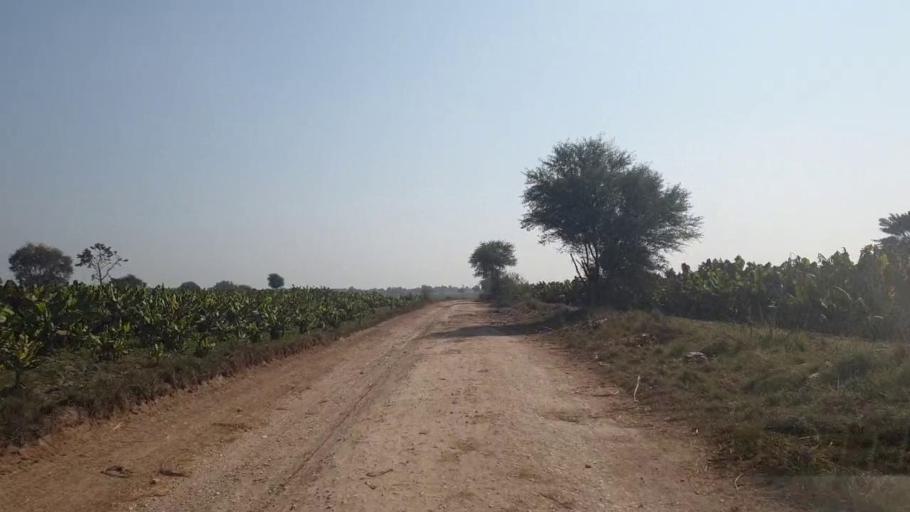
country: PK
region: Sindh
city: Sakrand
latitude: 26.0525
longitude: 68.4502
